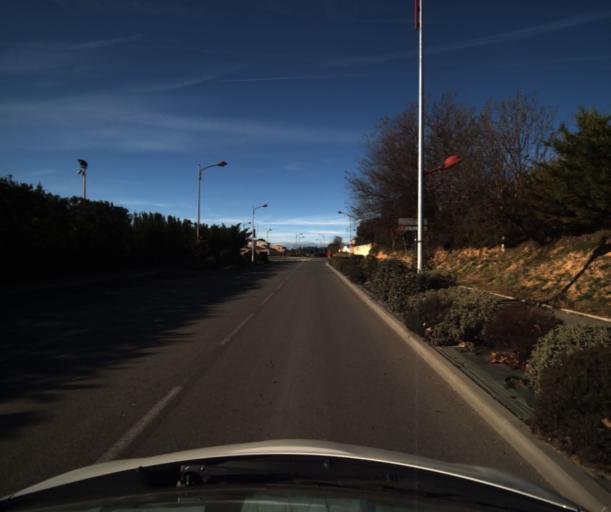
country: FR
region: Provence-Alpes-Cote d'Azur
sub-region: Departement du Vaucluse
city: Pertuis
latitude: 43.6949
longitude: 5.4873
